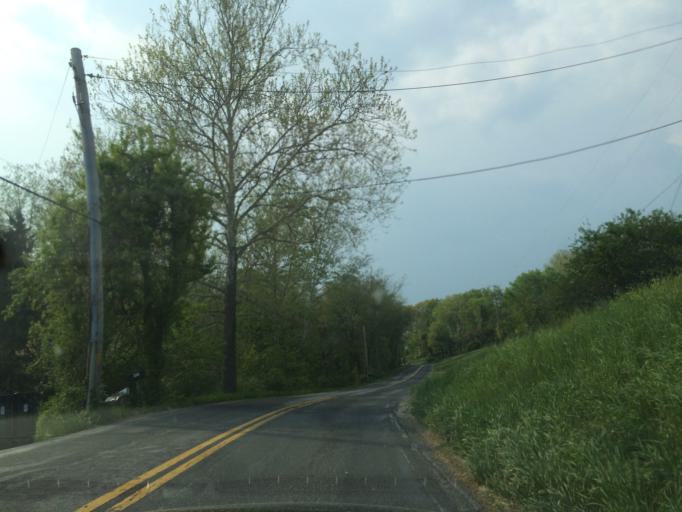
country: US
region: Maryland
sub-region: Carroll County
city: Mount Airy
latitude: 39.3632
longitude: -77.1388
